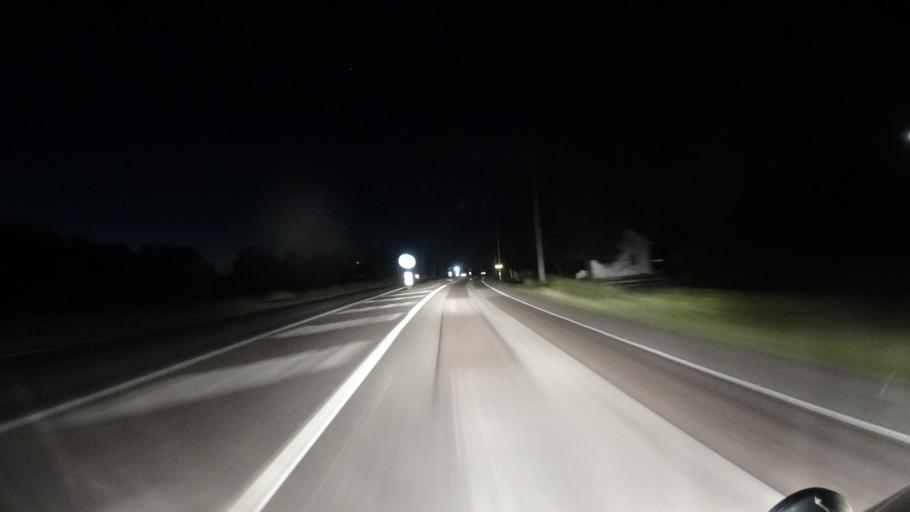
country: SE
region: OEstergoetland
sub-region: Odeshogs Kommun
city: OEdeshoeg
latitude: 58.2576
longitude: 14.7370
